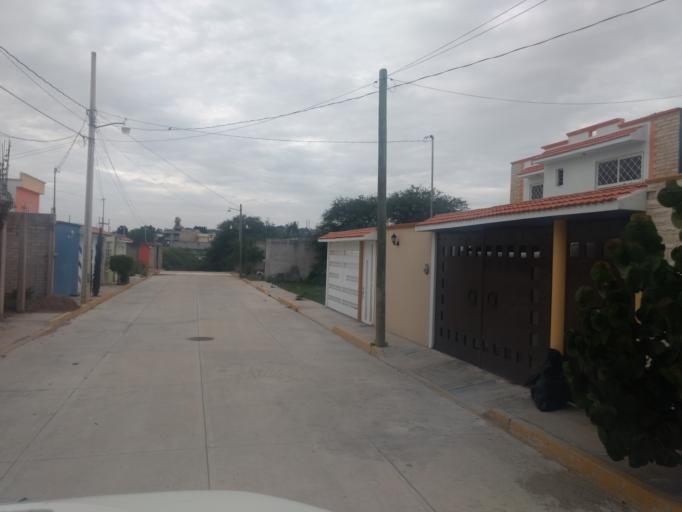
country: MX
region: Oaxaca
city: Ciudad de Huajuapam de Leon
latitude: 17.8065
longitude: -97.7918
